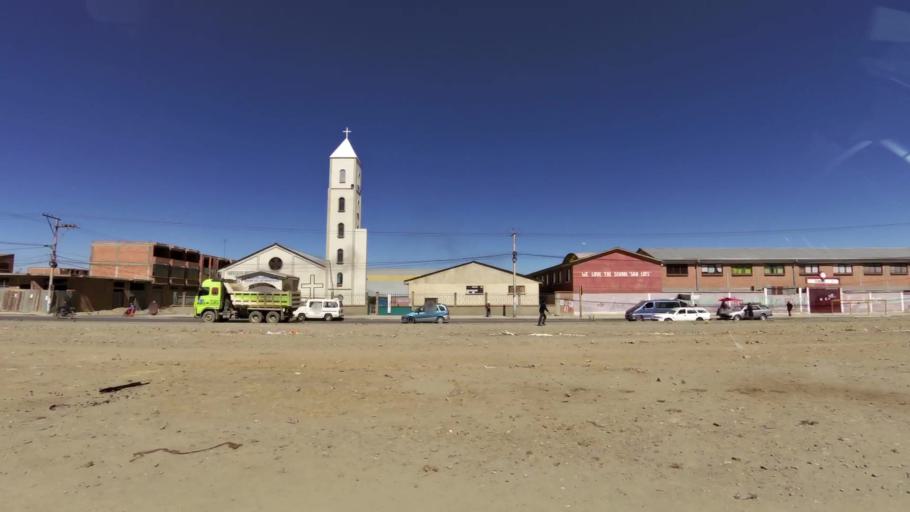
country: BO
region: La Paz
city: La Paz
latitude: -16.5437
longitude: -68.2016
